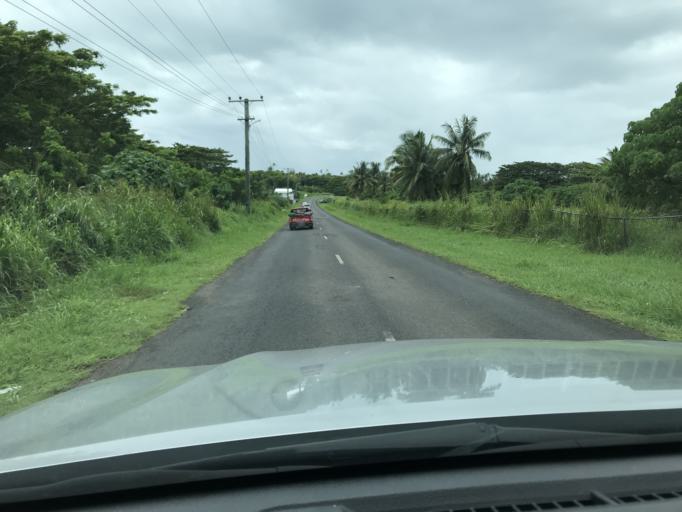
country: WS
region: Aiga-i-le-Tai
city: Mulifanua
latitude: -13.8326
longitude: -172.0275
